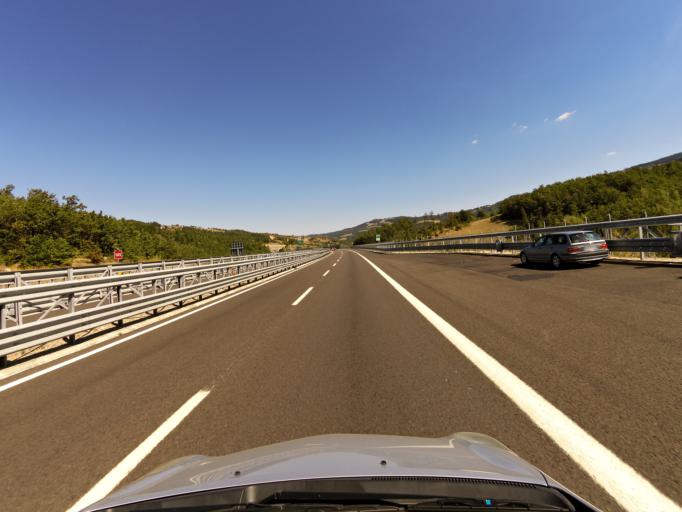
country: IT
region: Emilia-Romagna
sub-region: Provincia di Bologna
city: Castiglione dei Pepoli
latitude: 44.1592
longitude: 11.1968
